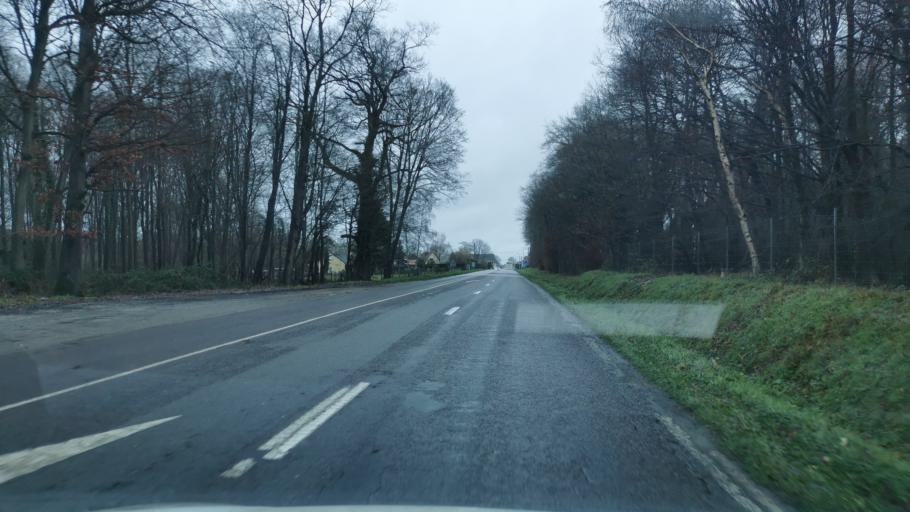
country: FR
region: Haute-Normandie
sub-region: Departement de l'Eure
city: Normanville
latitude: 49.0771
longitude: 1.1785
